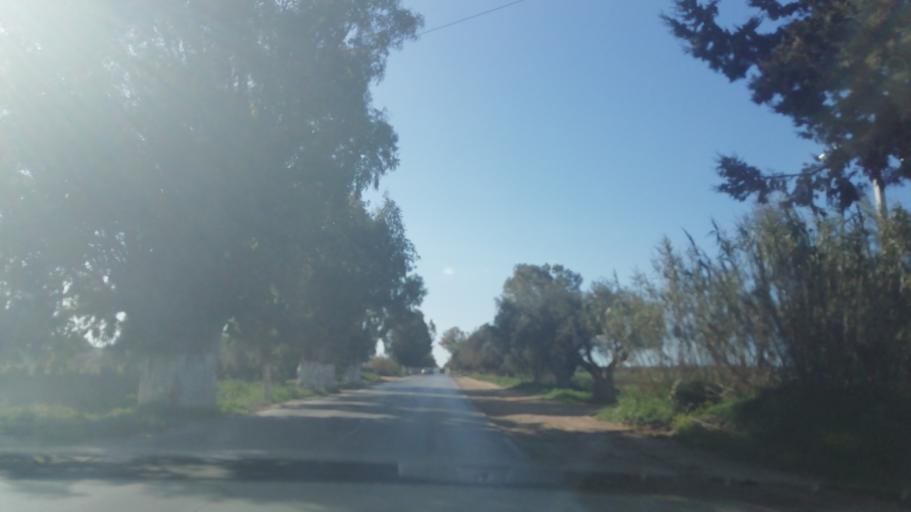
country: DZ
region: Mostaganem
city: Mostaganem
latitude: 35.9986
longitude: 0.3189
